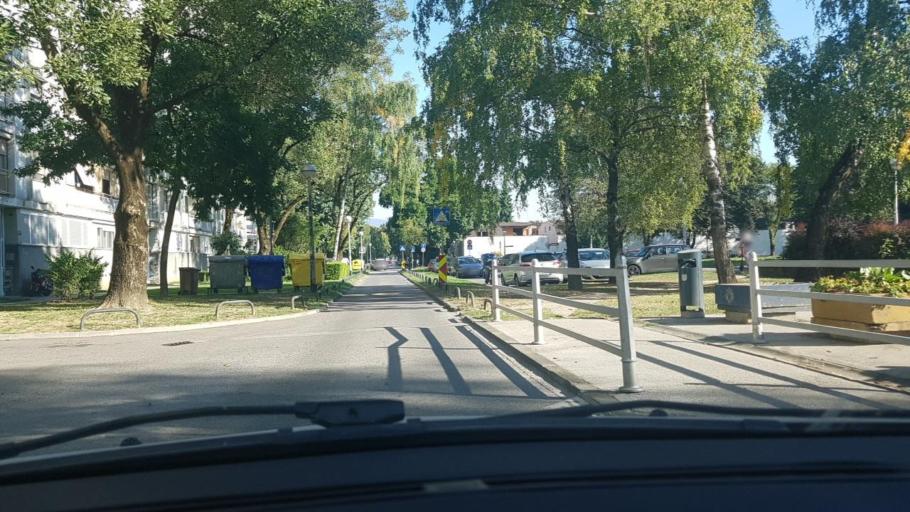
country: HR
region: Grad Zagreb
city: Novi Zagreb
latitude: 45.7726
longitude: 15.9706
